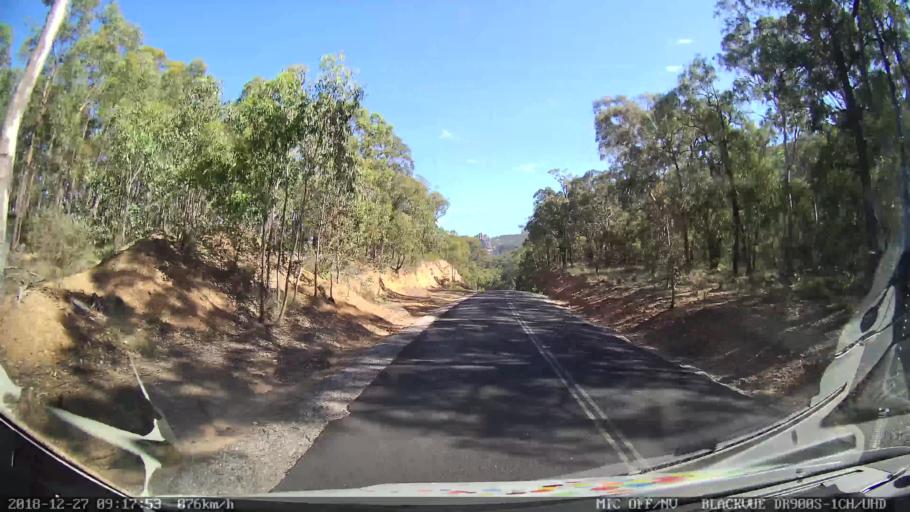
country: AU
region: New South Wales
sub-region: Lithgow
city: Portland
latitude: -33.1330
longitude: 150.0461
